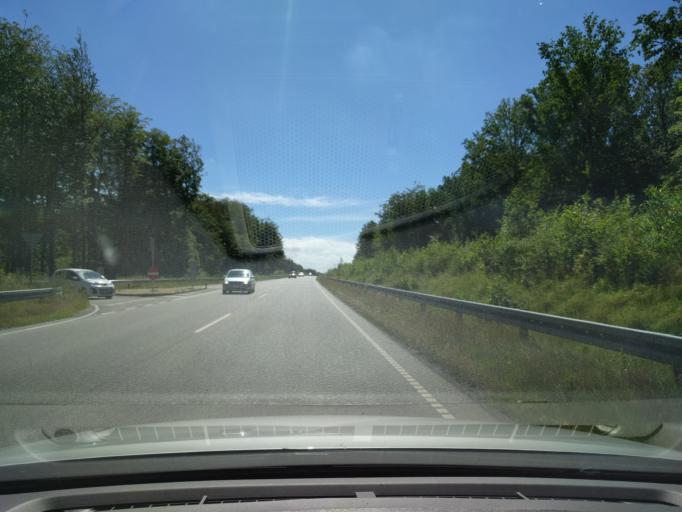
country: DK
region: Zealand
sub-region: Naestved Kommune
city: Naestved
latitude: 55.2391
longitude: 11.7978
